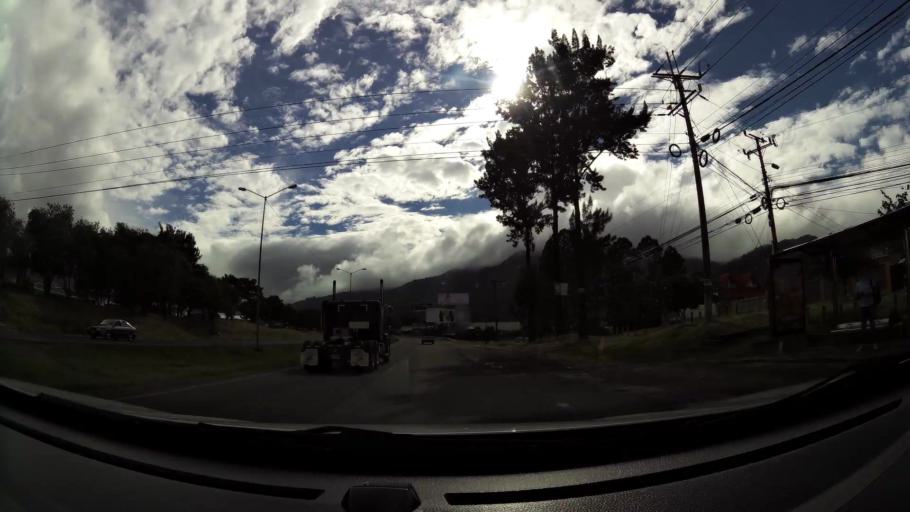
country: CR
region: Cartago
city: San Diego
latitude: 9.9013
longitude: -84.0057
